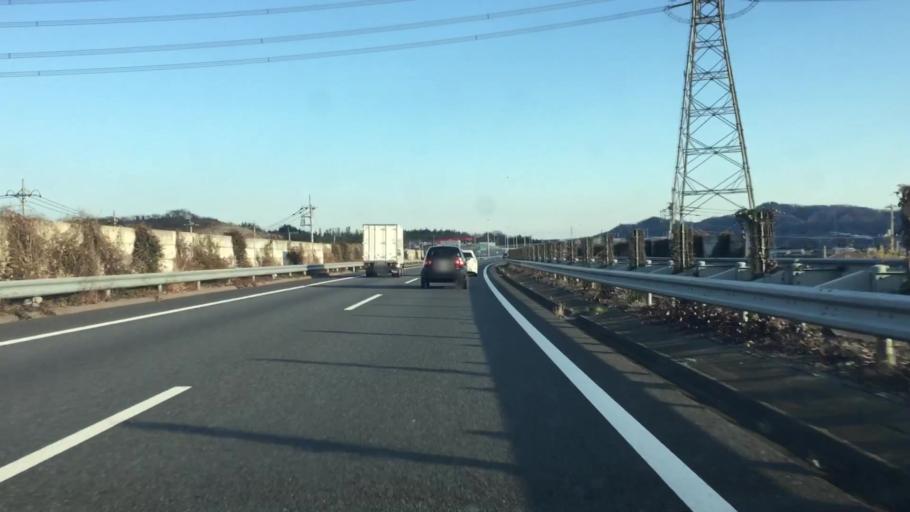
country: JP
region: Gunma
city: Ota
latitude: 36.3424
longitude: 139.3413
